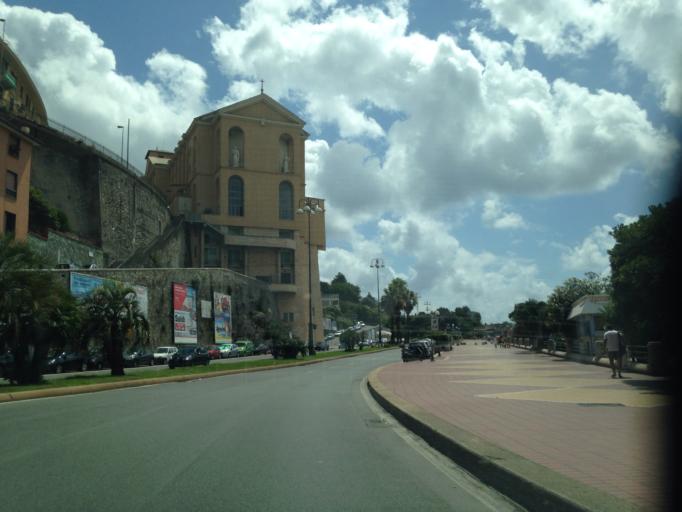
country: IT
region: Liguria
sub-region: Provincia di Genova
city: San Teodoro
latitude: 44.3949
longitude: 8.9491
